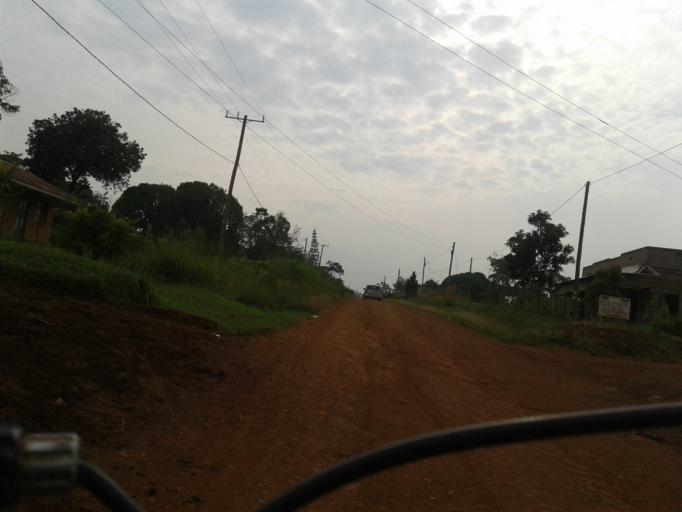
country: UG
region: Western Region
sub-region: Hoima District
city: Hoima
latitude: 1.4278
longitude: 31.3299
